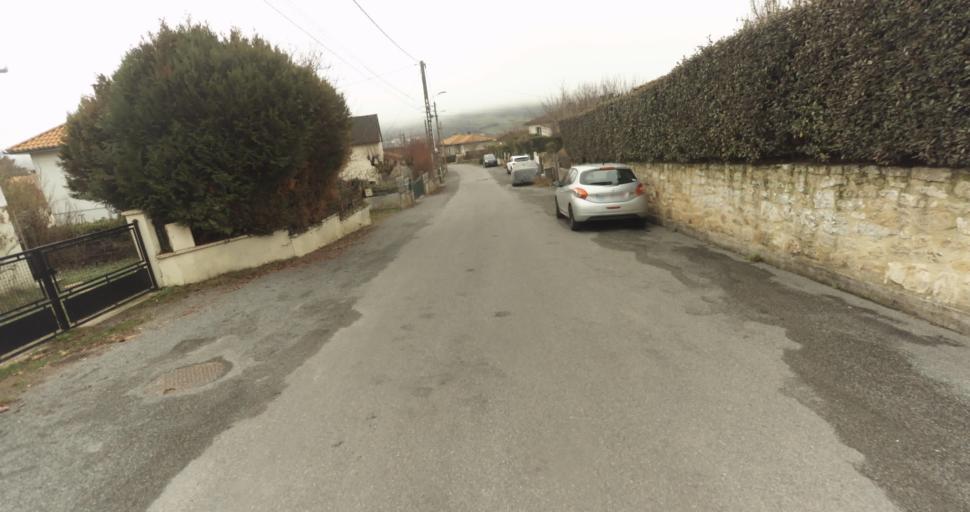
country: FR
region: Midi-Pyrenees
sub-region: Departement du Lot
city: Figeac
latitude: 44.6130
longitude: 2.0399
